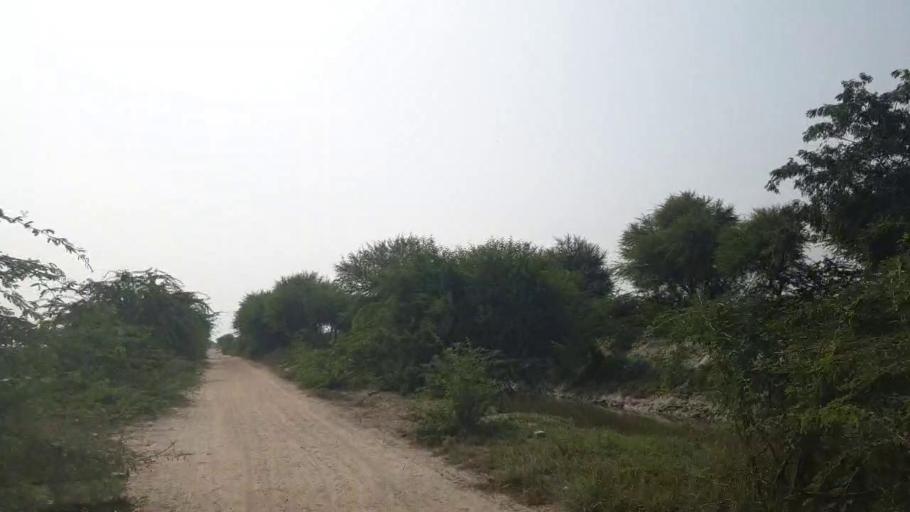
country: PK
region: Sindh
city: Badin
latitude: 24.6087
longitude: 68.7208
